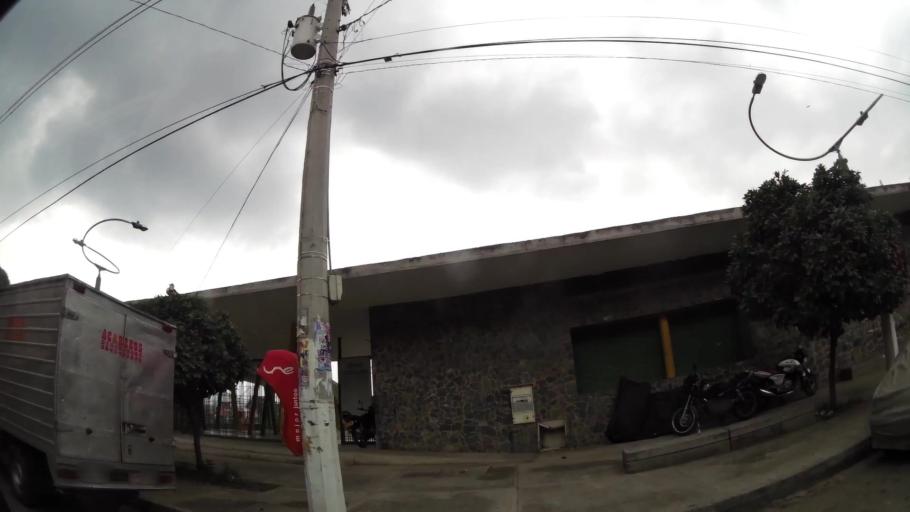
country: CO
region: Antioquia
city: Medellin
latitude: 6.2739
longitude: -75.5966
